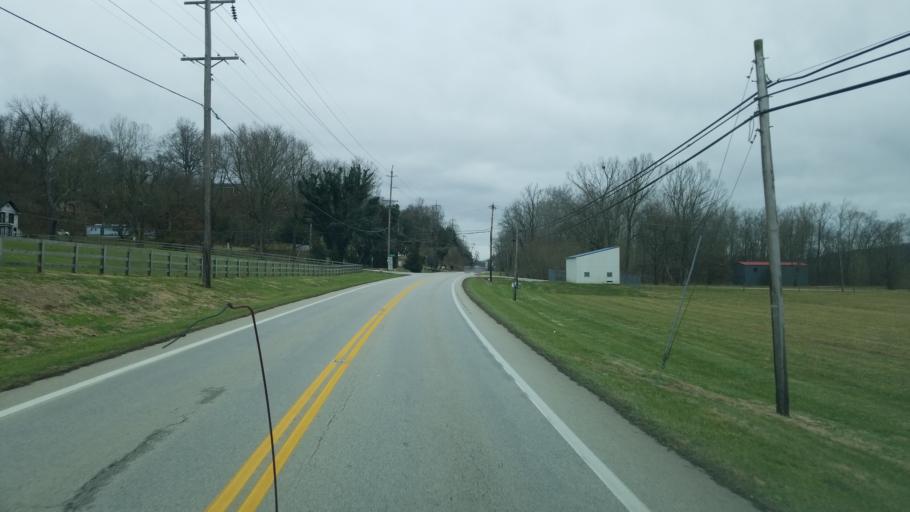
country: US
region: Ohio
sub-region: Clermont County
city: New Richmond
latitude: 38.9235
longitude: -84.2542
